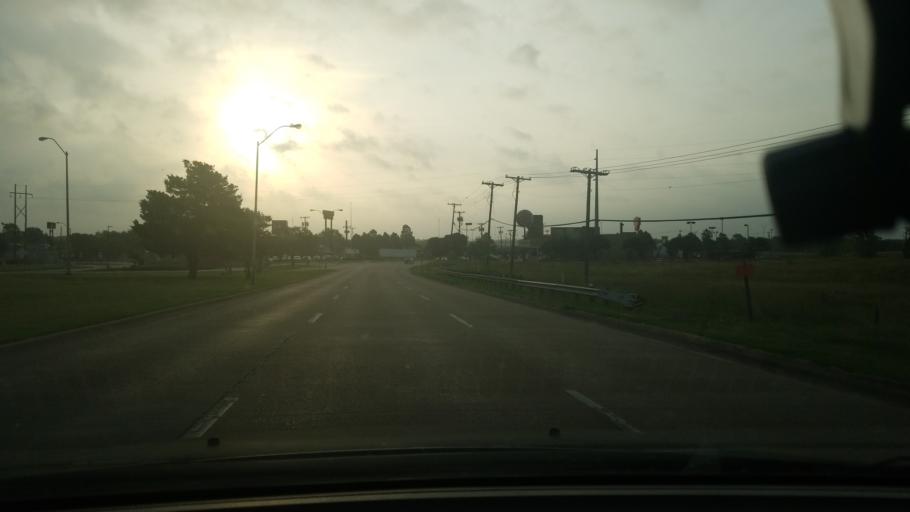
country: US
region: Texas
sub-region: Dallas County
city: Mesquite
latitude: 32.7675
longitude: -96.6263
